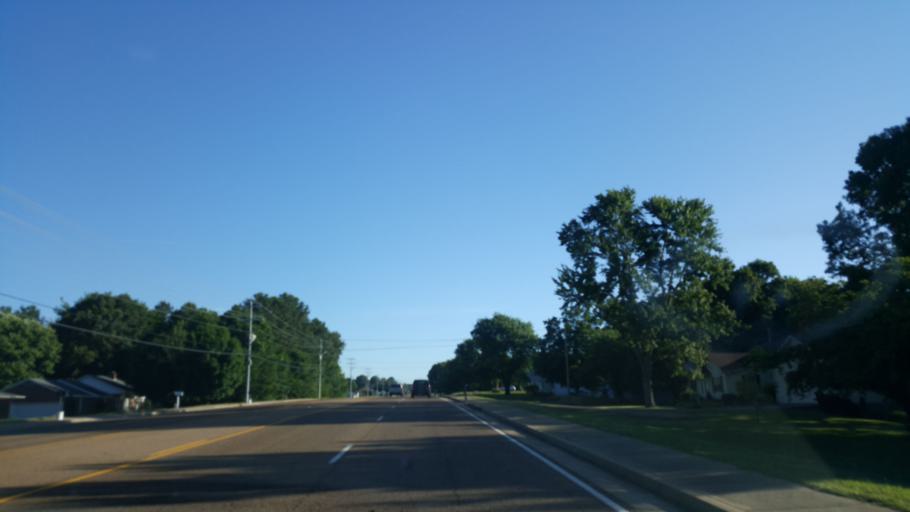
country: US
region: Tennessee
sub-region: Henderson County
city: Lexington
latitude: 35.6740
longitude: -88.3849
